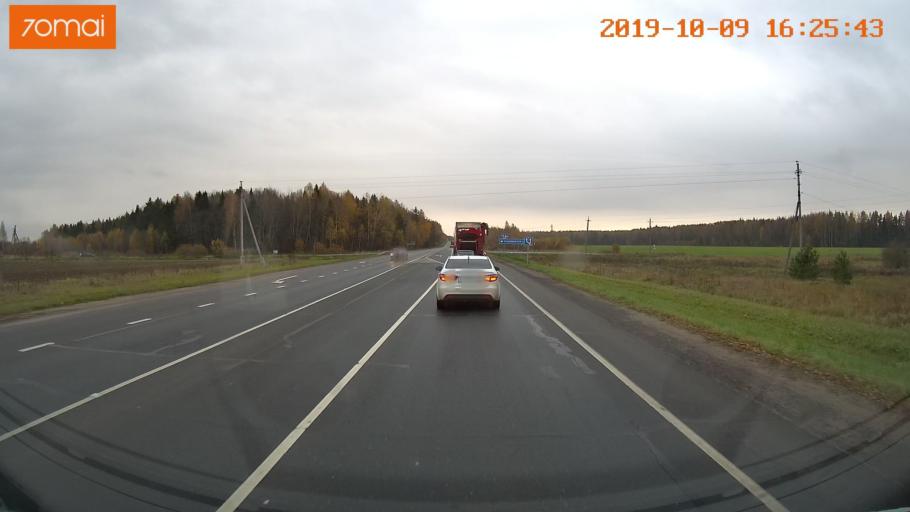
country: RU
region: Kostroma
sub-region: Kostromskoy Rayon
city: Kostroma
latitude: 57.6409
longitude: 40.9210
